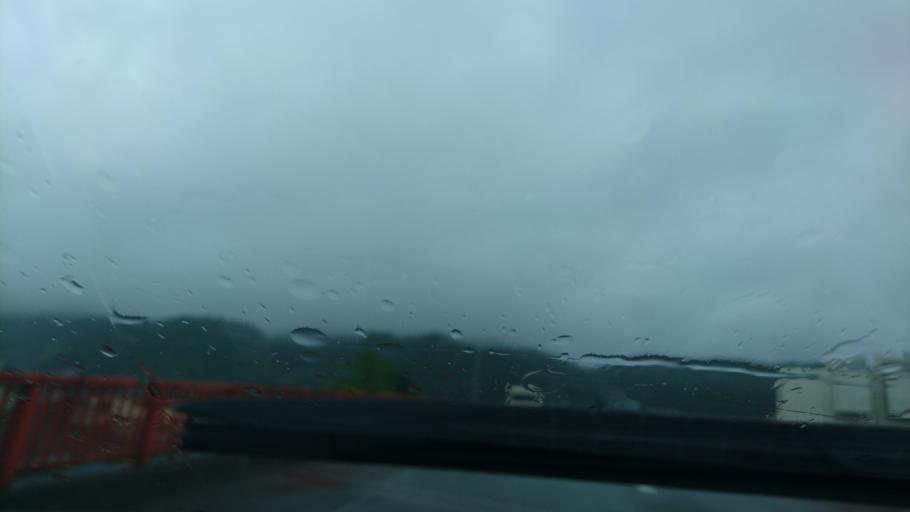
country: JP
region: Miyagi
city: Ishinomaki
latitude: 38.4399
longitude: 141.3143
